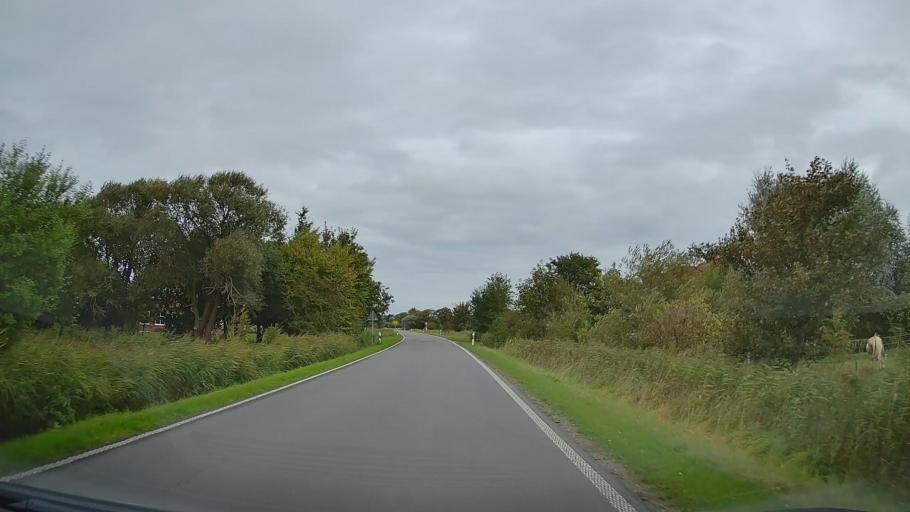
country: DE
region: Schleswig-Holstein
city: Klanxbull
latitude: 54.8718
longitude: 8.6820
